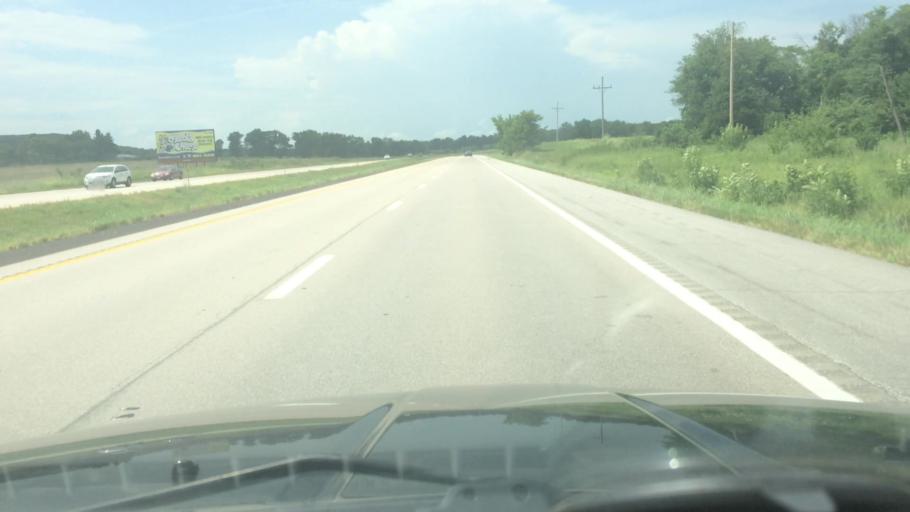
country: US
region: Missouri
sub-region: Polk County
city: Humansville
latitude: 37.8150
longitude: -93.6089
